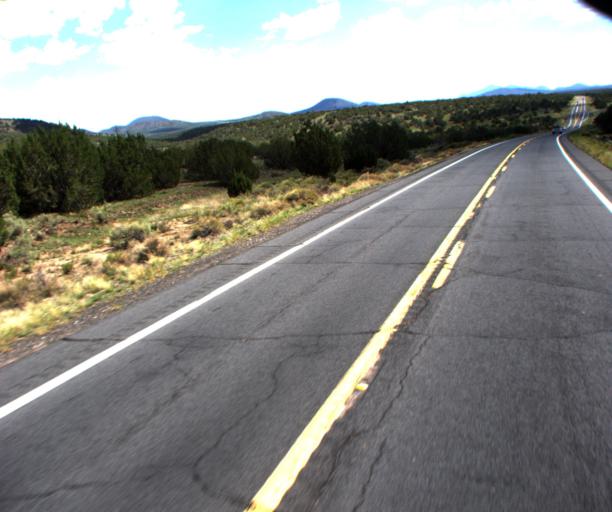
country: US
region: Arizona
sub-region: Coconino County
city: Williams
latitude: 35.4881
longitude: -112.1748
